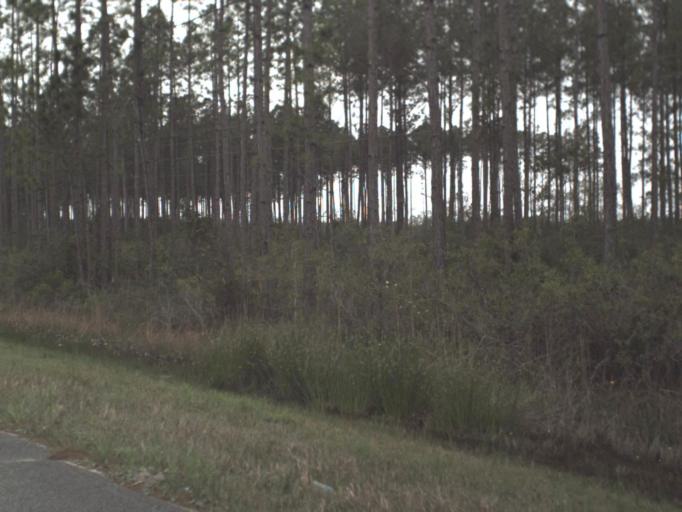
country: US
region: Florida
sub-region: Gulf County
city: Port Saint Joe
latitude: 29.9249
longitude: -85.1967
